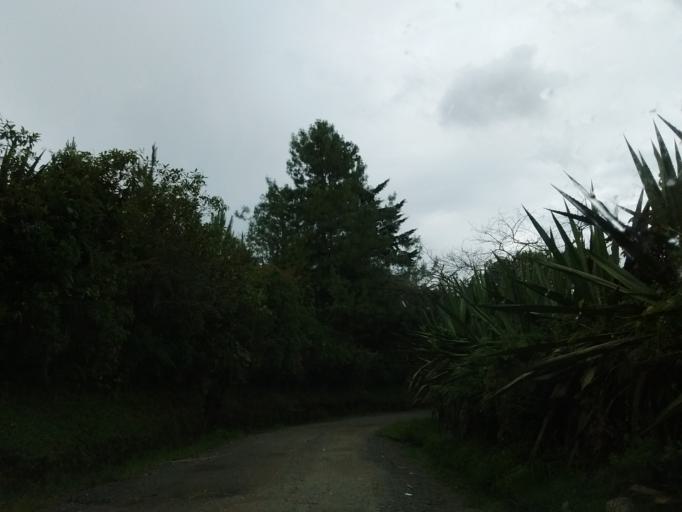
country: CO
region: Cauca
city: Cajibio
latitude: 2.5798
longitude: -76.6611
